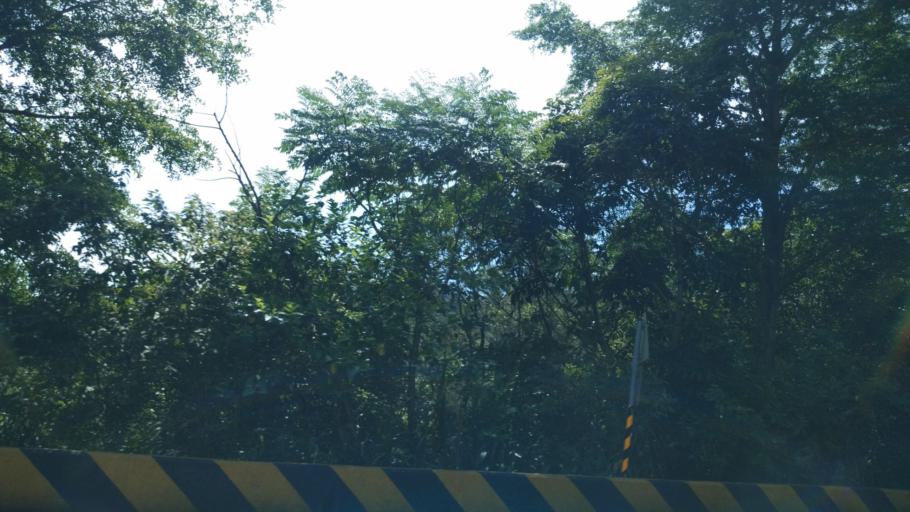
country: TW
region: Taipei
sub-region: Taipei
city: Banqiao
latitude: 24.9453
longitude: 121.5042
